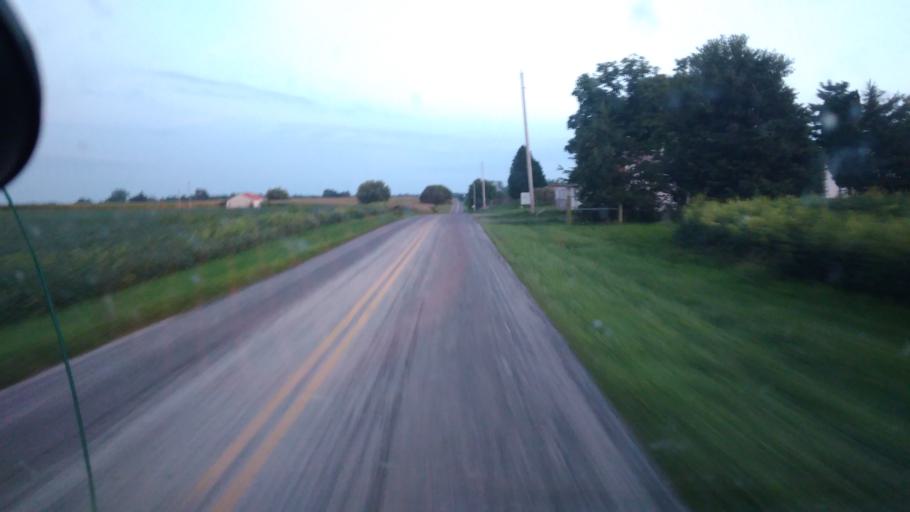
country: US
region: Ohio
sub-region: Hardin County
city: Kenton
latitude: 40.6311
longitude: -83.4573
